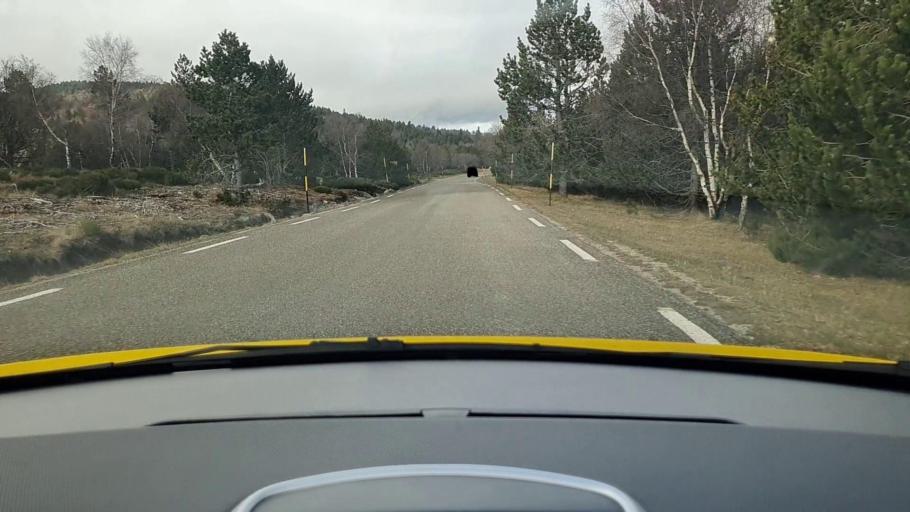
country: FR
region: Languedoc-Roussillon
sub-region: Departement du Gard
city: Branoux-les-Taillades
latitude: 44.3899
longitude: 3.8952
